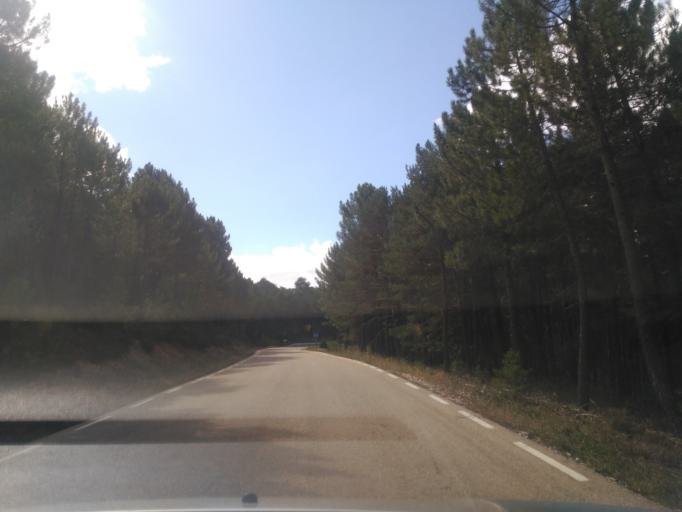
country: ES
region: Castille and Leon
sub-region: Provincia de Soria
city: Espejon
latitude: 41.8421
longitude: -3.2375
